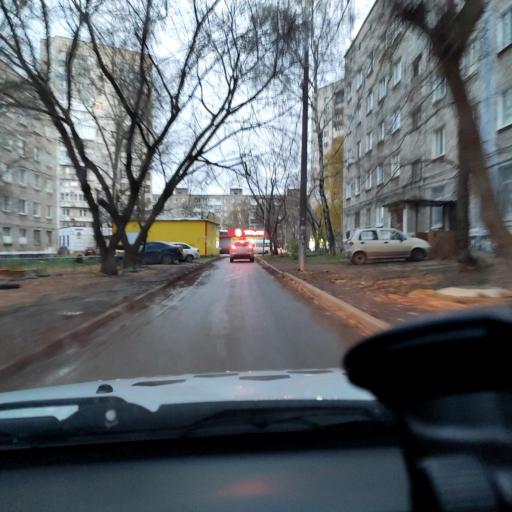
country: RU
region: Perm
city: Perm
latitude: 57.9778
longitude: 56.2312
